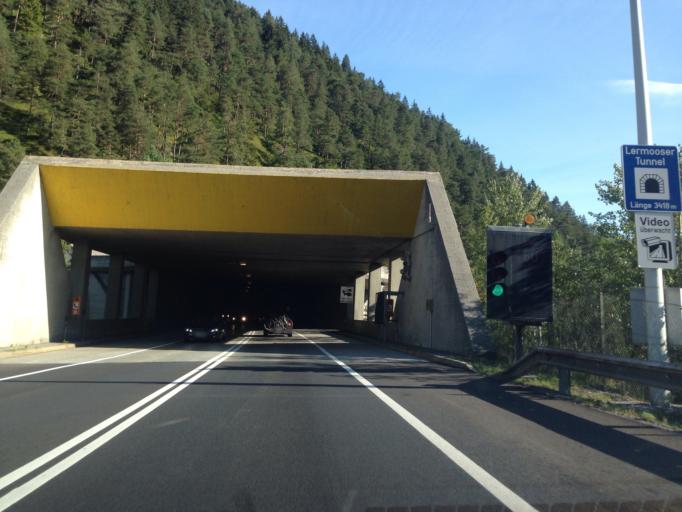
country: AT
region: Tyrol
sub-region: Politischer Bezirk Reutte
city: Biberwier
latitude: 47.3750
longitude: 10.8827
